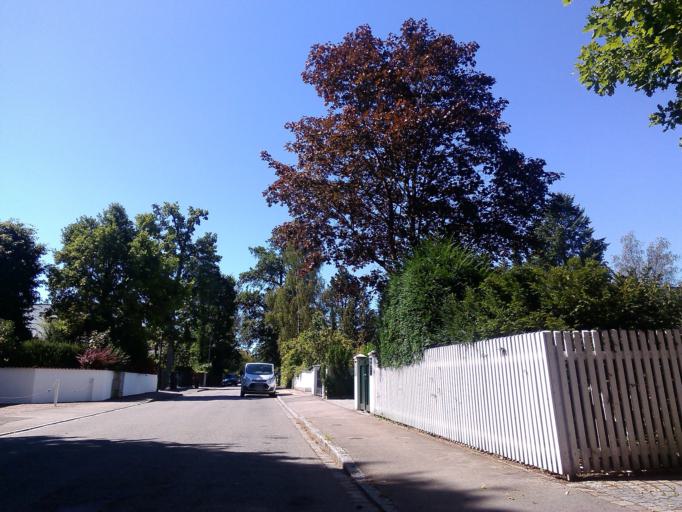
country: DE
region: Bavaria
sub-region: Upper Bavaria
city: Grafelfing
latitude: 48.1174
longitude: 11.4178
